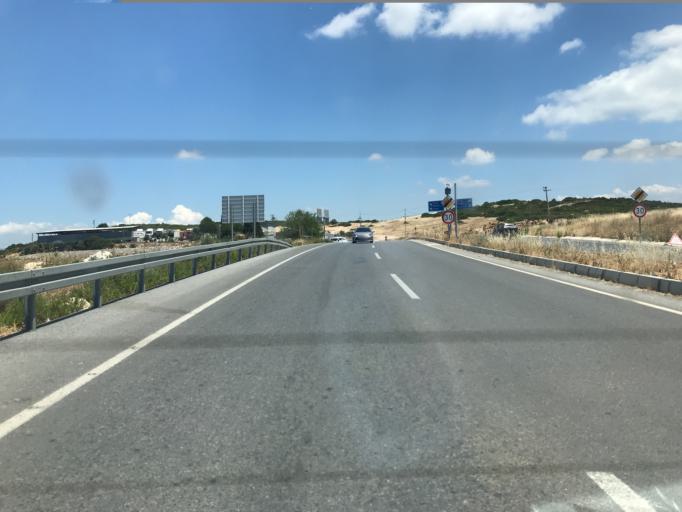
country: TR
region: Aydin
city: Akkoy
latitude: 37.4772
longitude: 27.3407
